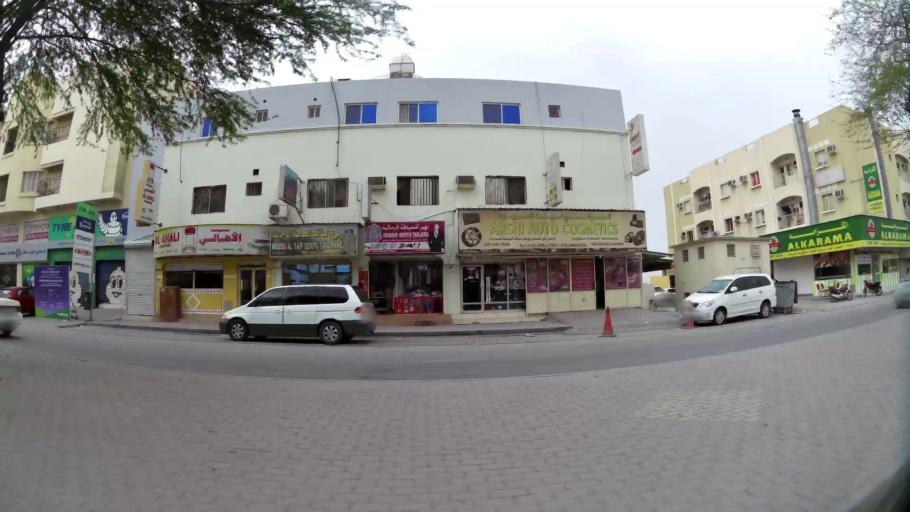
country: BH
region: Northern
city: Ar Rifa'
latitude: 26.1149
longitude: 50.5758
